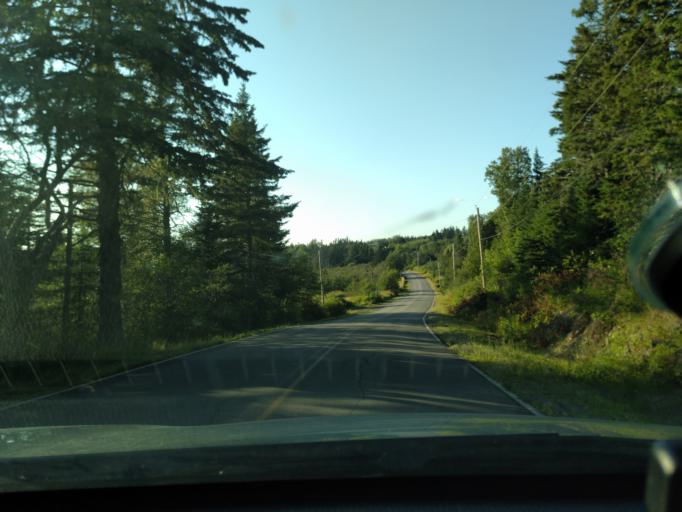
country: US
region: Maine
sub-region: Washington County
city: Machiasport
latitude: 44.6639
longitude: -67.2375
